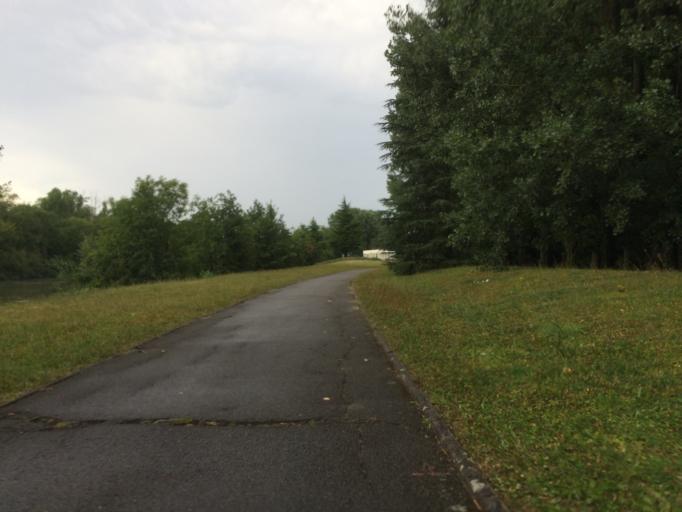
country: FR
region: Picardie
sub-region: Departement de l'Oise
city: Jaux
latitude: 49.3877
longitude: 2.7808
